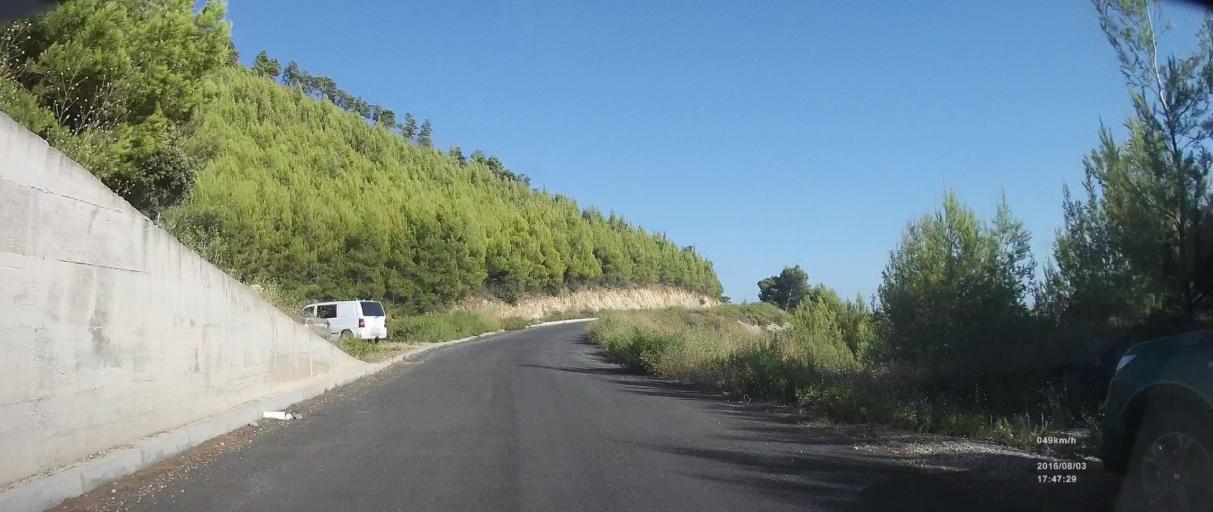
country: HR
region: Dubrovacko-Neretvanska
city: Blato
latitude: 42.7377
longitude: 17.5023
